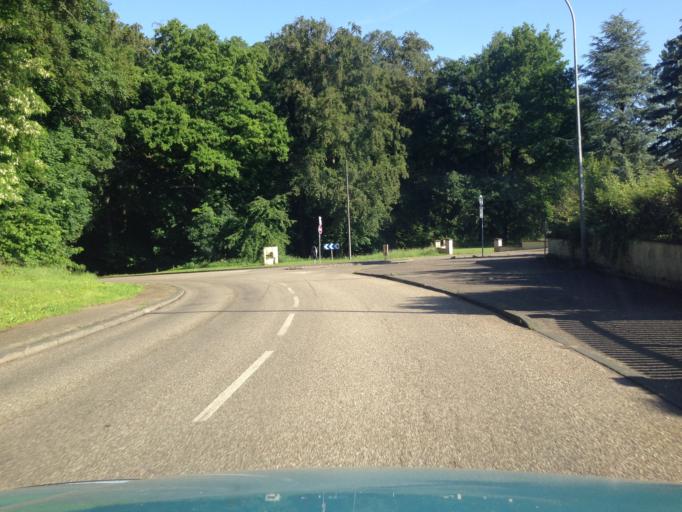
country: FR
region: Alsace
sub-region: Departement du Bas-Rhin
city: Ingwiller
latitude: 48.8761
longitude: 7.4710
